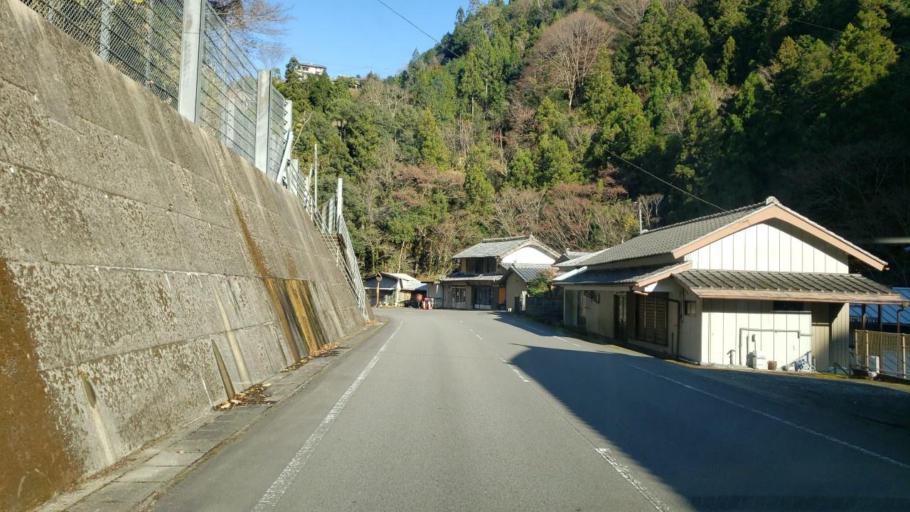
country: JP
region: Tokushima
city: Wakimachi
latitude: 34.0116
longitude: 134.0312
